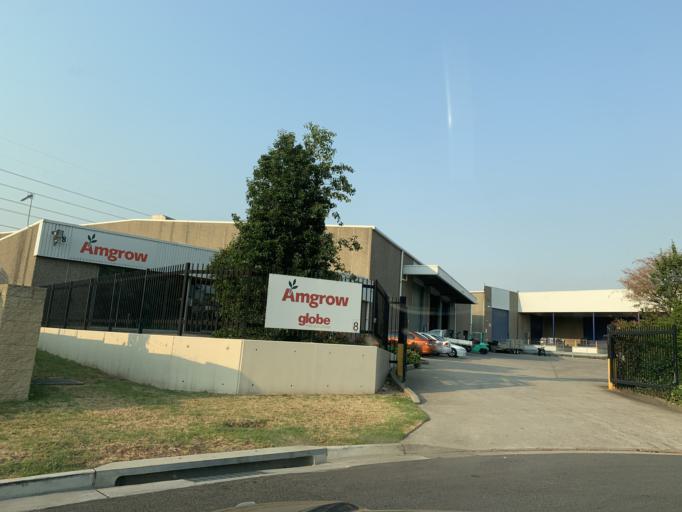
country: AU
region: New South Wales
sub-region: Fairfield
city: Horsley Park
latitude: -33.8402
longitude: 150.8887
